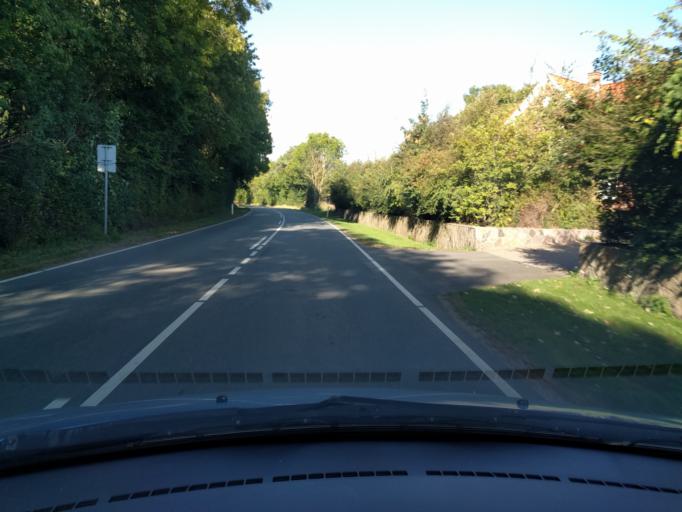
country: DK
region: South Denmark
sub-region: Assens Kommune
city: Assens
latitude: 55.2095
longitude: 9.9968
